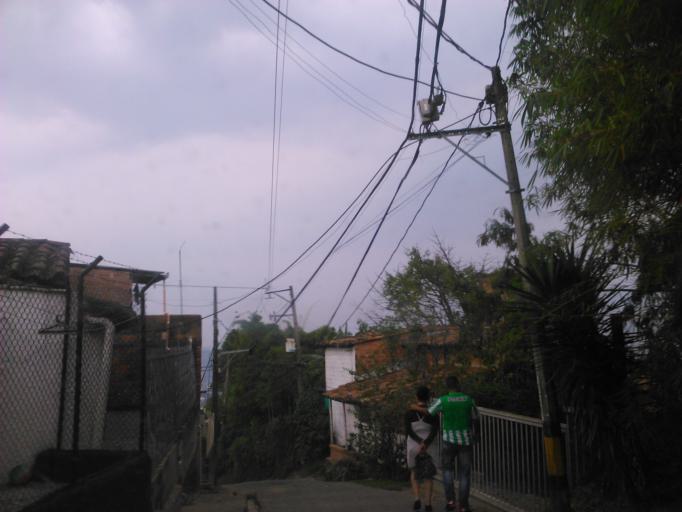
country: CO
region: Antioquia
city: La Estrella
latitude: 6.1394
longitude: -75.6390
